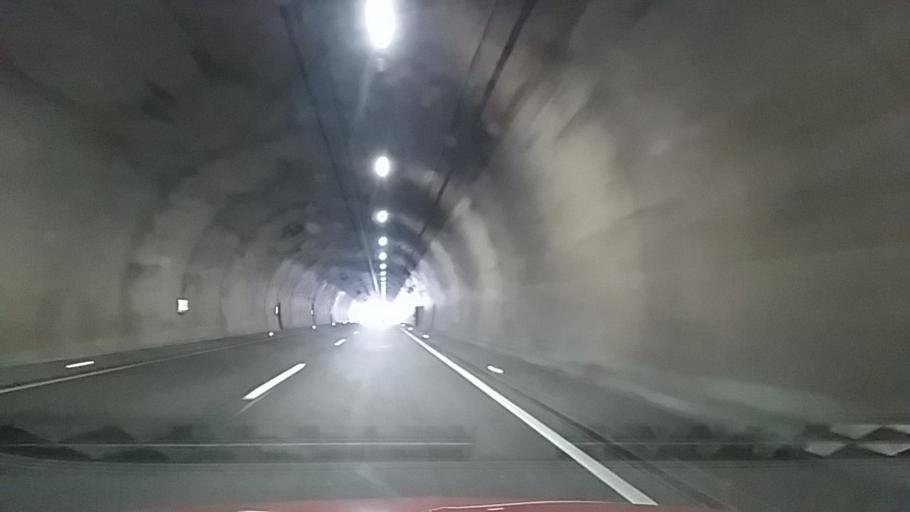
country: DE
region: Thuringia
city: Zella-Mehlis
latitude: 50.6555
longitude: 10.6900
